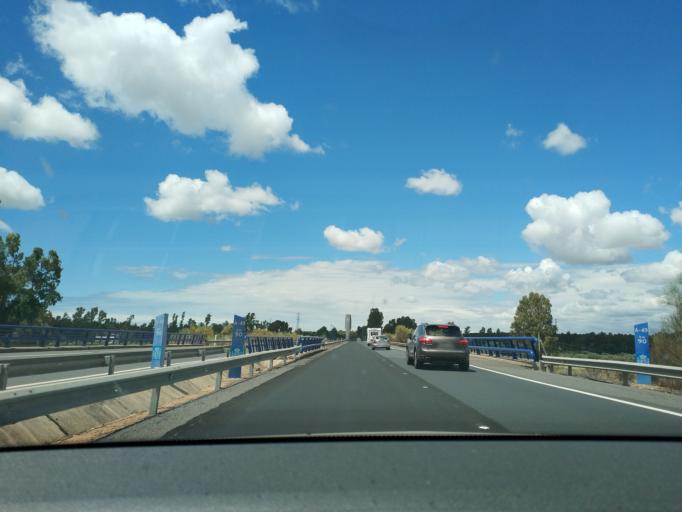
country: ES
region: Andalusia
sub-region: Provincia de Huelva
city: Gibraleon
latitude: 37.3520
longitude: -6.9808
